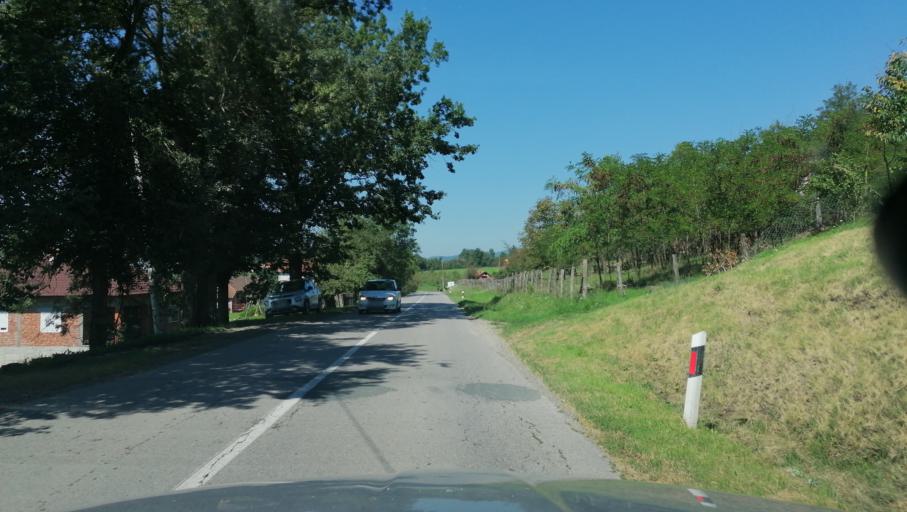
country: RS
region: Central Serbia
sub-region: Raski Okrug
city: Vrnjacka Banja
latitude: 43.7052
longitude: 20.8470
